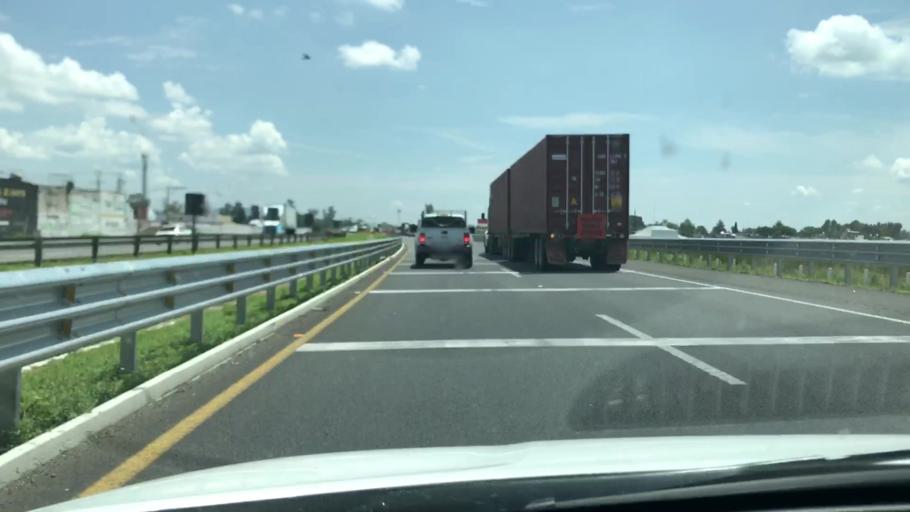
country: MX
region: Guanajuato
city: Irapuato
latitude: 20.6486
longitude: -101.3517
